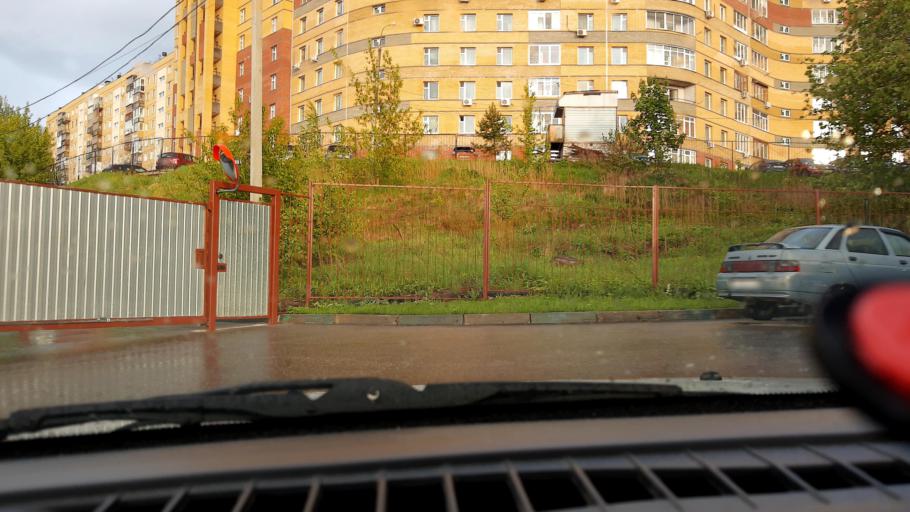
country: RU
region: Nizjnij Novgorod
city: Afonino
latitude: 56.2877
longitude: 44.0643
